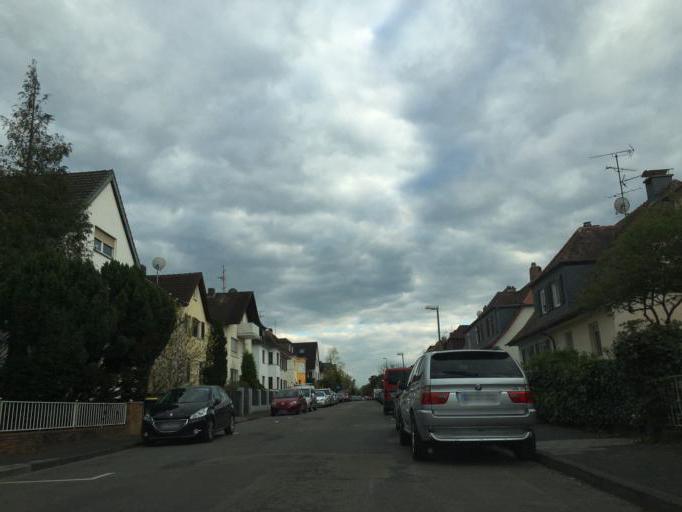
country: DE
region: Hesse
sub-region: Regierungsbezirk Darmstadt
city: Offenbach
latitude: 50.0955
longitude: 8.7918
